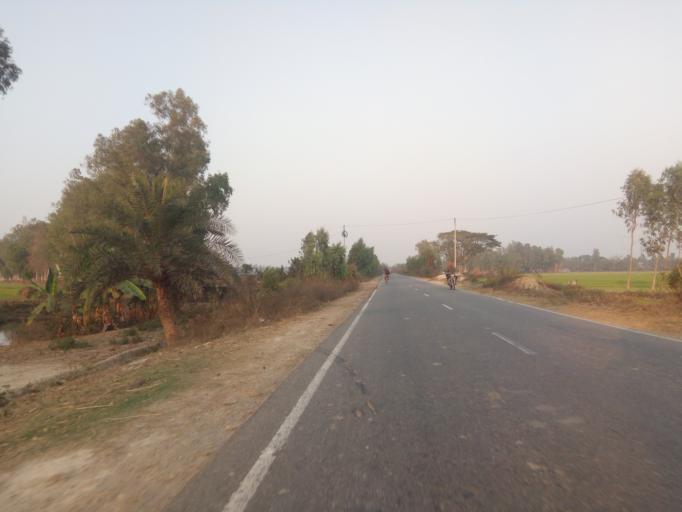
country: BD
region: Rajshahi
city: Bogra
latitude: 24.5840
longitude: 89.2281
